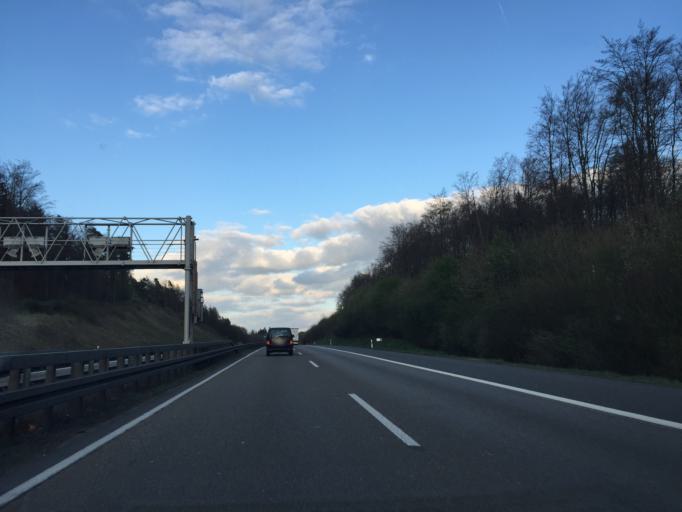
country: DE
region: Hesse
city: Kirtorf
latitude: 50.7154
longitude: 9.1266
